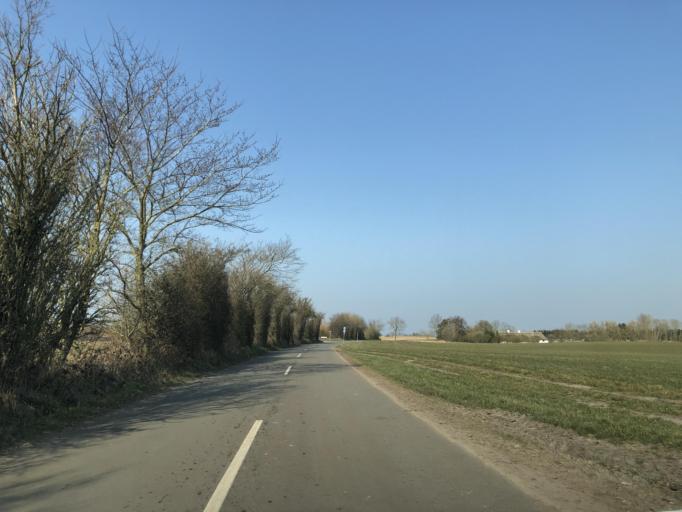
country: DK
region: South Denmark
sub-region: Sonderborg Kommune
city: Nordborg
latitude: 55.0698
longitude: 9.7308
